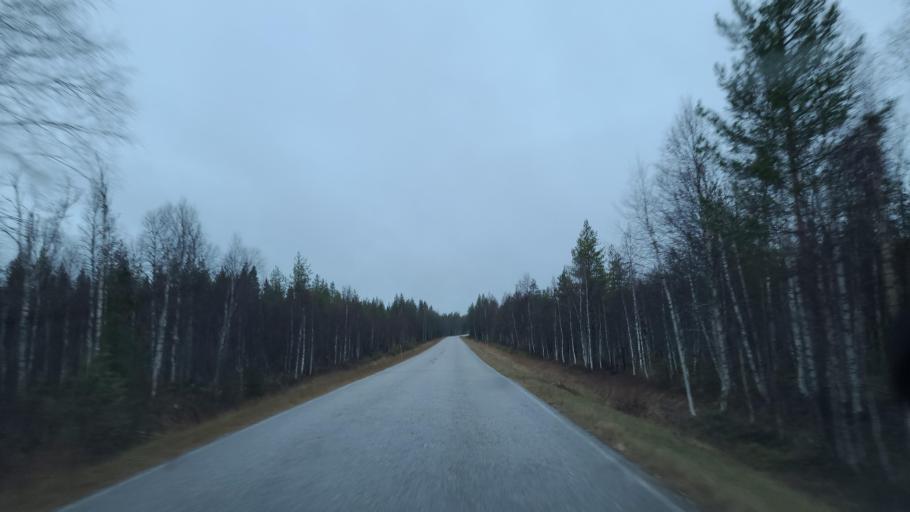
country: FI
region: Lapland
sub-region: Kemi-Tornio
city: Simo
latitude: 65.8994
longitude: 25.2083
